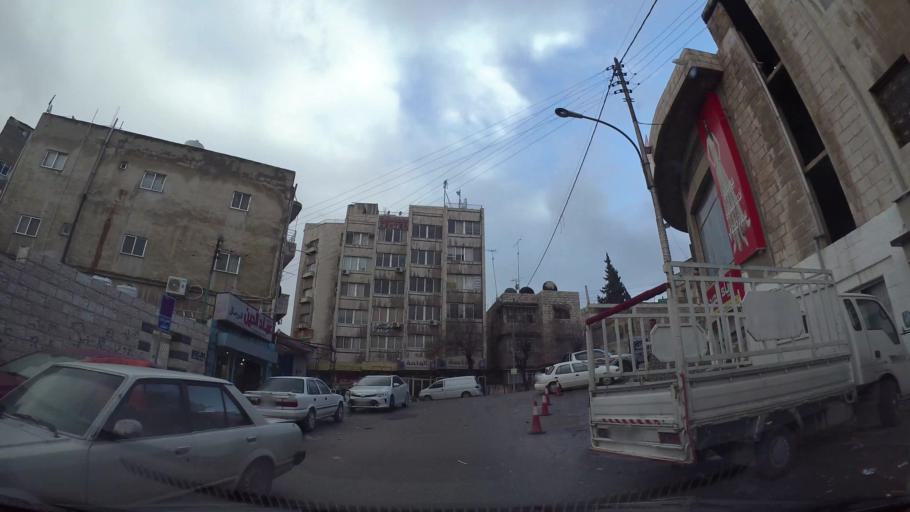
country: JO
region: Amman
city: Amman
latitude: 31.9625
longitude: 35.9251
